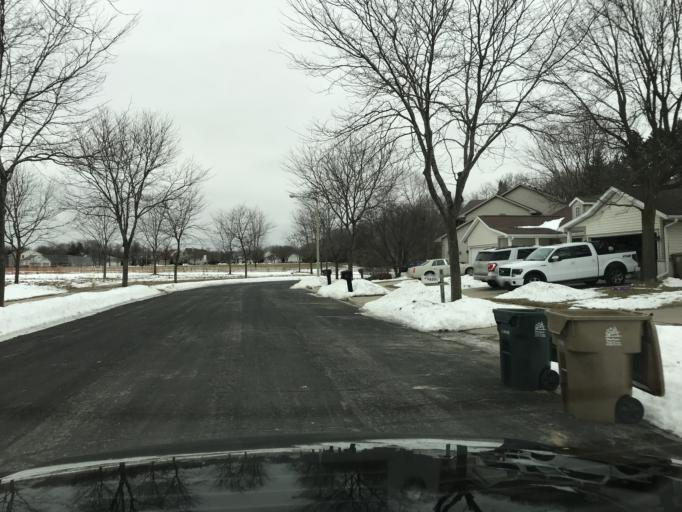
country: US
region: Wisconsin
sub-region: Dane County
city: Monona
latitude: 43.0773
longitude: -89.2722
